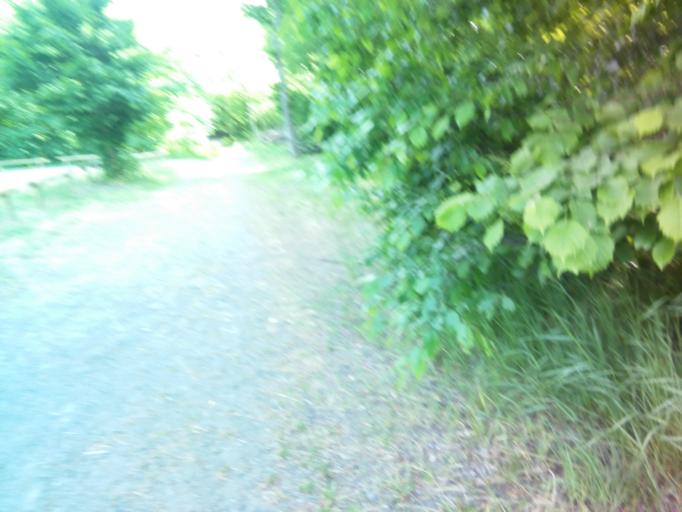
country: DK
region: Capital Region
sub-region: Bornholm Kommune
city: Akirkeby
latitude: 55.2270
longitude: 14.8845
